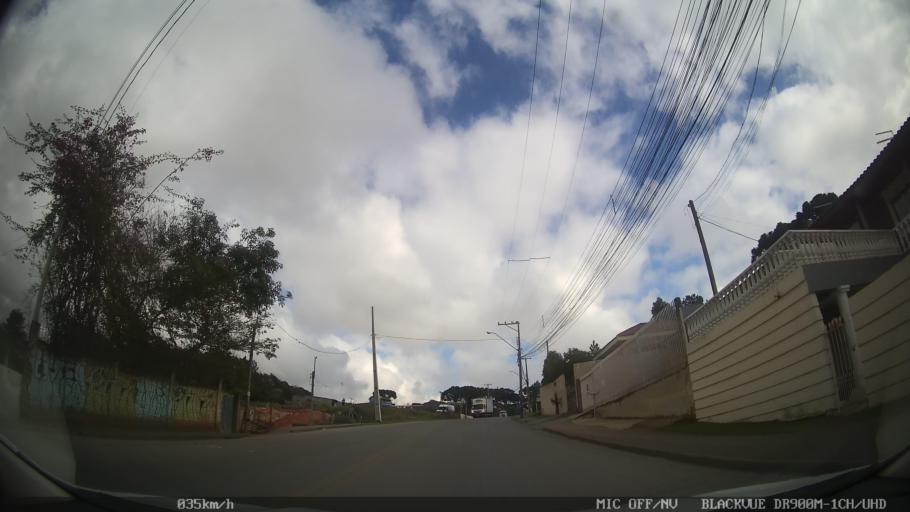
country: BR
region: Parana
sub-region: Colombo
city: Colombo
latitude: -25.3429
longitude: -49.2411
